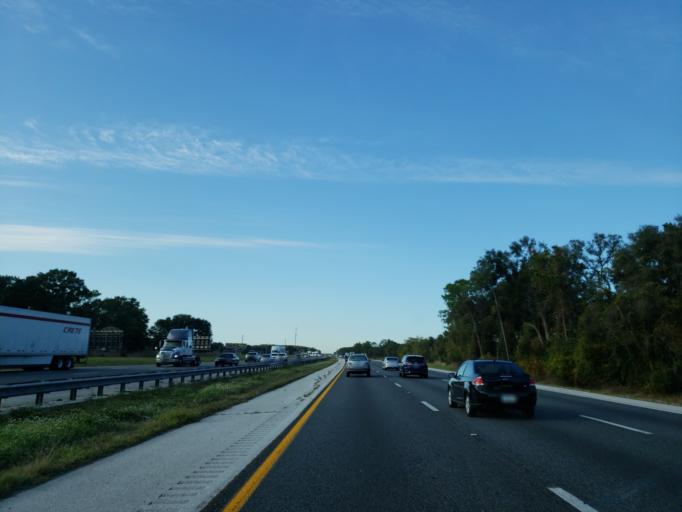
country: US
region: Florida
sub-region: Marion County
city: Belleview
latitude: 28.9656
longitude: -82.1266
